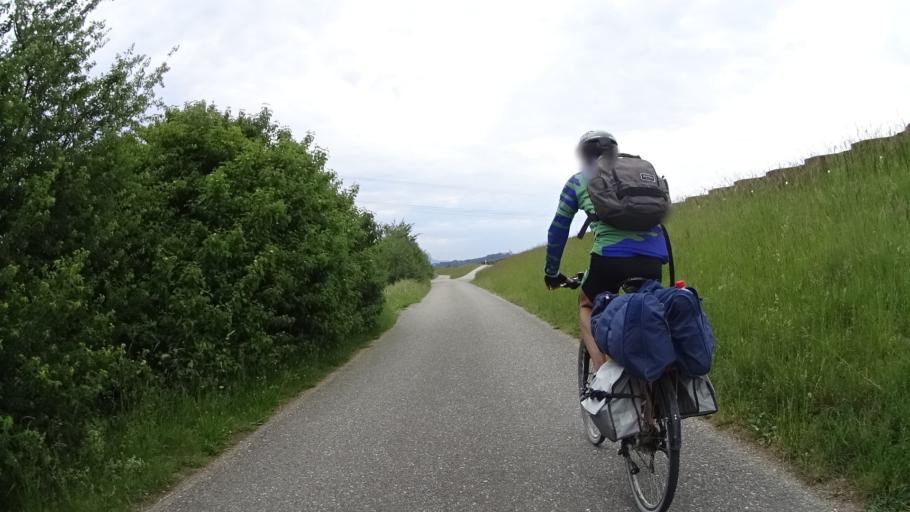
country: DE
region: Bavaria
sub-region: Lower Bavaria
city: Parkstetten
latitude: 48.9094
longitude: 12.6380
